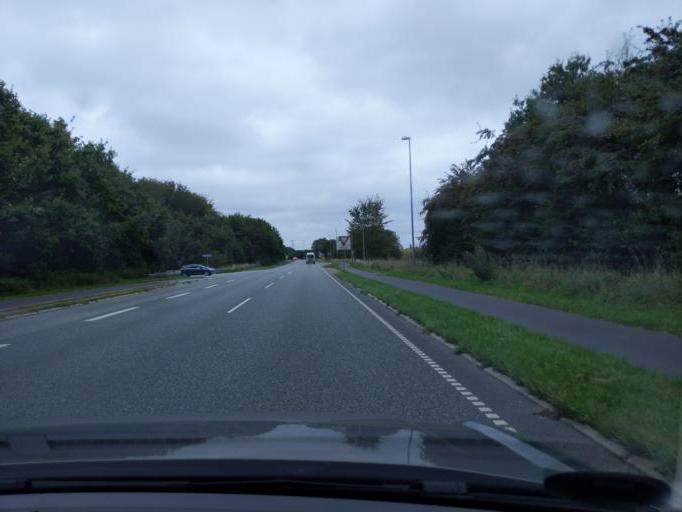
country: DK
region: Central Jutland
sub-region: Randers Kommune
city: Randers
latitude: 56.4853
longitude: 9.9908
